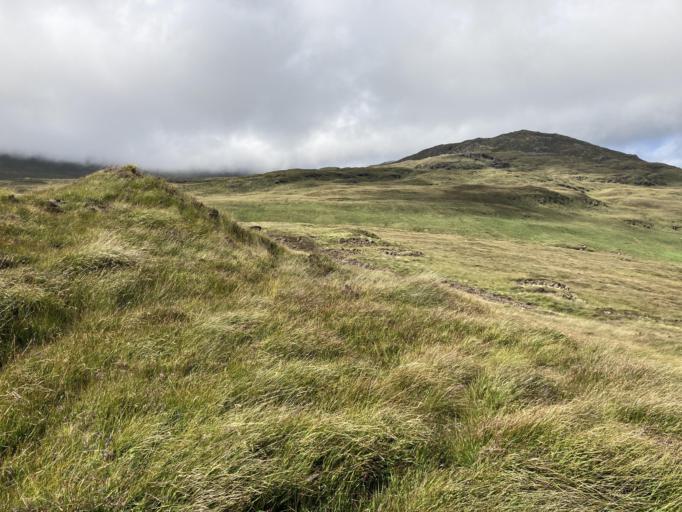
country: GB
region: Scotland
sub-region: Highland
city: Isle of Skye
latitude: 57.0159
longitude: -6.3390
